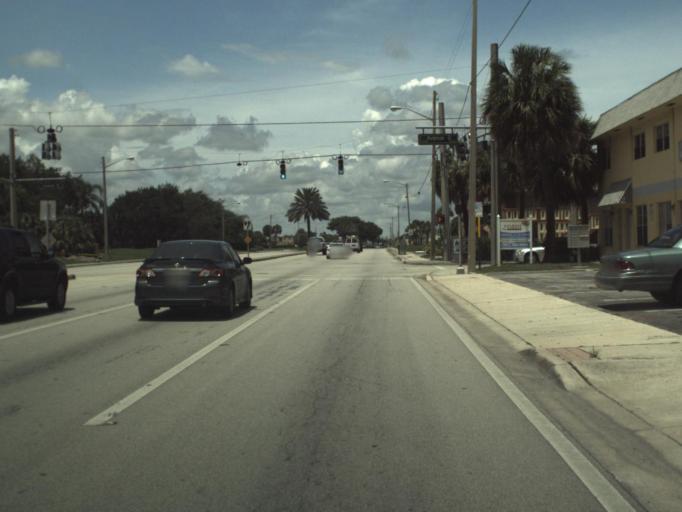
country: US
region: Florida
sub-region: Palm Beach County
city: Riviera Beach
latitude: 26.7810
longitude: -80.0729
